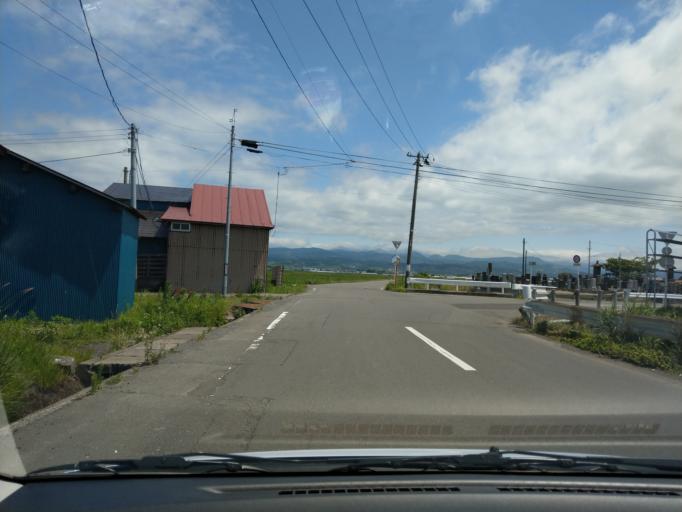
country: JP
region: Aomori
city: Namioka
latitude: 40.6833
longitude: 140.5597
